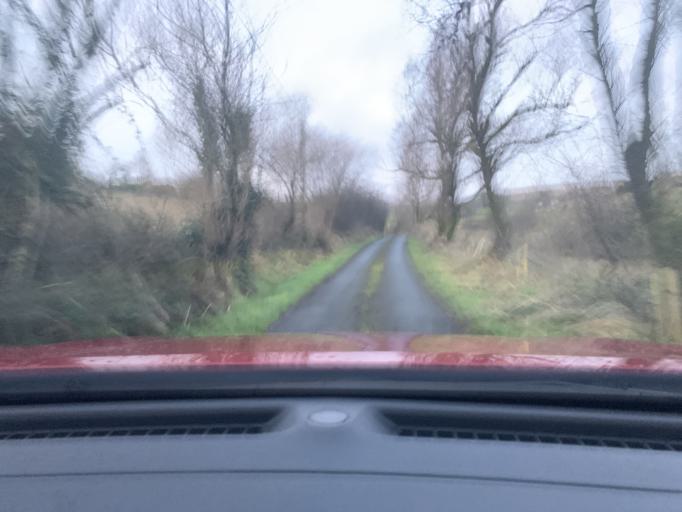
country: IE
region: Connaught
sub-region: Sligo
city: Ballymote
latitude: 54.0450
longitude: -8.4071
